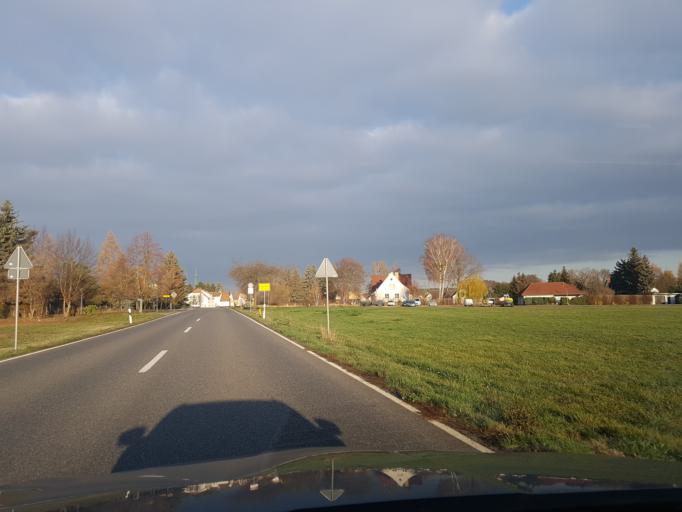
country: DE
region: Brandenburg
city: Luckau
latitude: 51.8759
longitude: 13.6952
